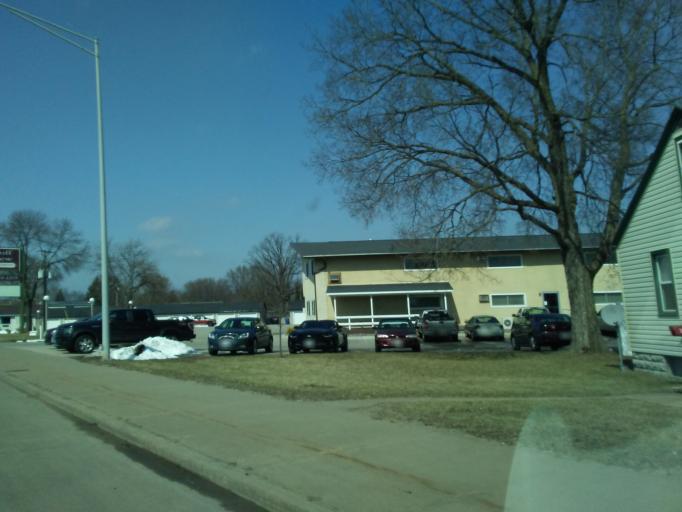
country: US
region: Wisconsin
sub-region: La Crosse County
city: La Crosse
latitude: 43.7774
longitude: -91.2221
